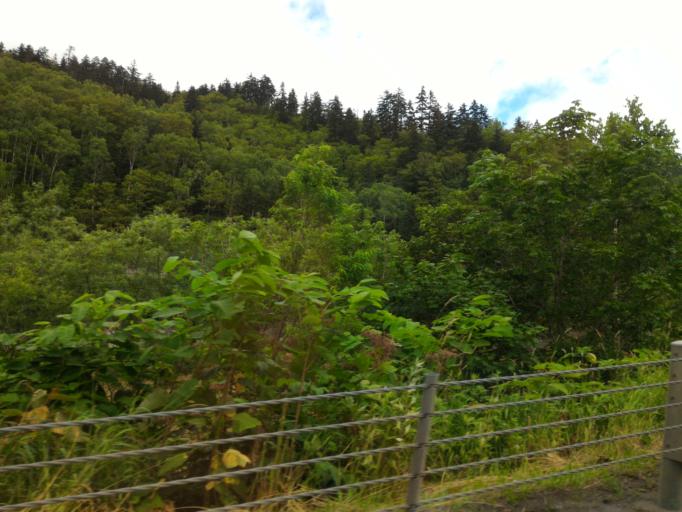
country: JP
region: Hokkaido
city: Nayoro
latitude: 44.7263
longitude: 142.2300
